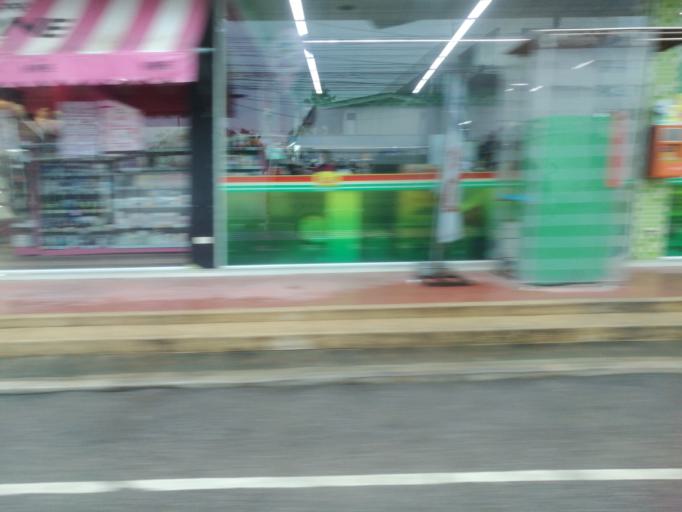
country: TH
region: Prachuap Khiri Khan
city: Prachuap Khiri Khan
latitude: 11.8094
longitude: 99.7958
